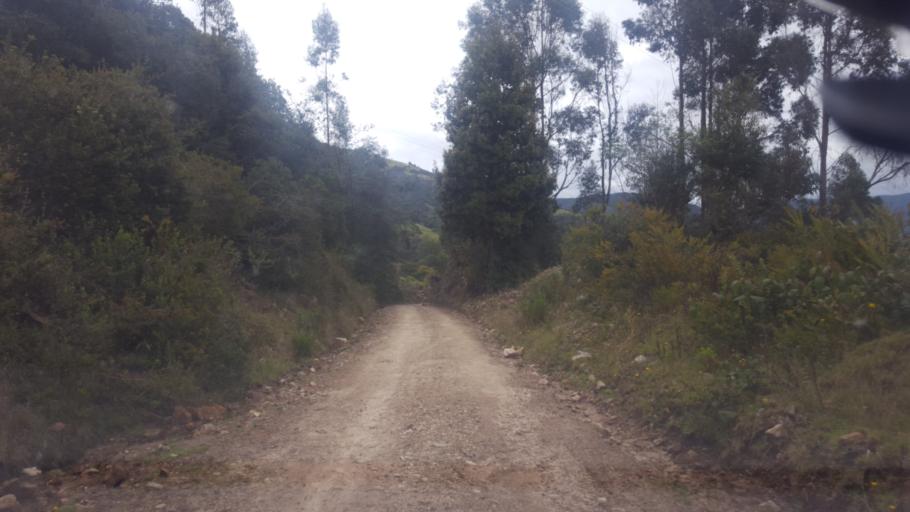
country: CO
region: Boyaca
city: Belen
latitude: 6.0301
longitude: -72.8824
